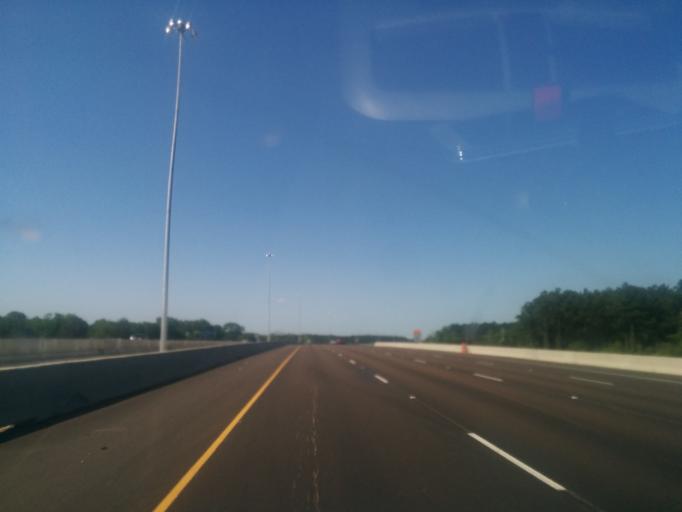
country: US
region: Mississippi
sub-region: Madison County
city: Ridgeland
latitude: 32.4473
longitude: -90.1446
